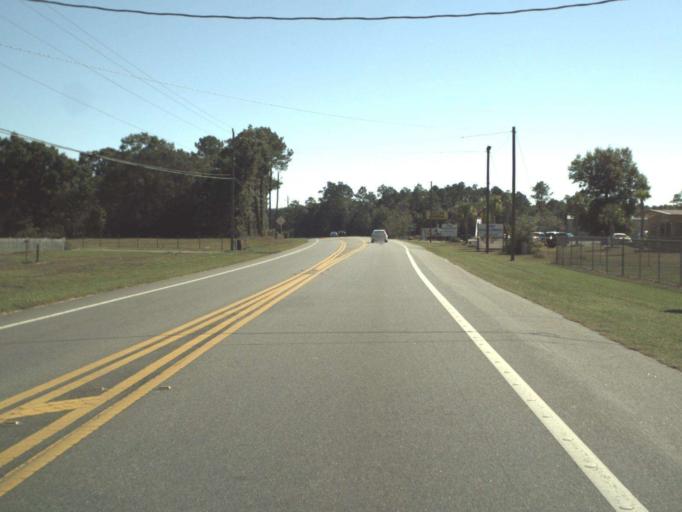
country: US
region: Florida
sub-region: Okaloosa County
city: Crestview
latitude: 30.7678
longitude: -86.6703
